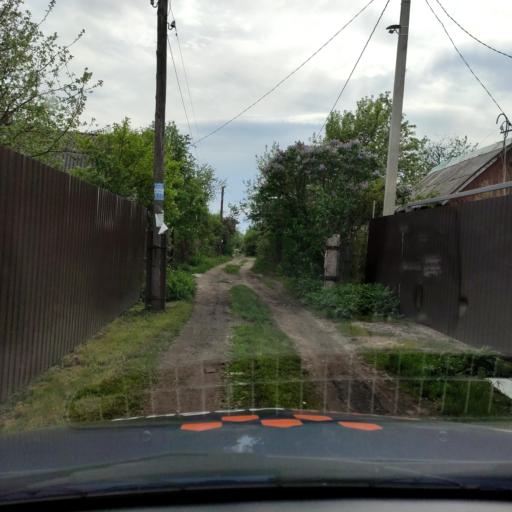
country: RU
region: Voronezj
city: Voronezh
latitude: 51.5975
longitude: 39.1543
